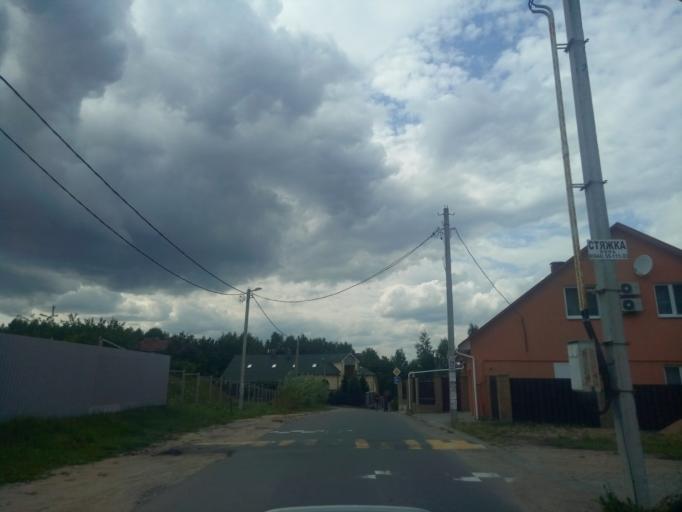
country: BY
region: Minsk
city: Zhdanovichy
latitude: 53.9376
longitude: 27.4221
